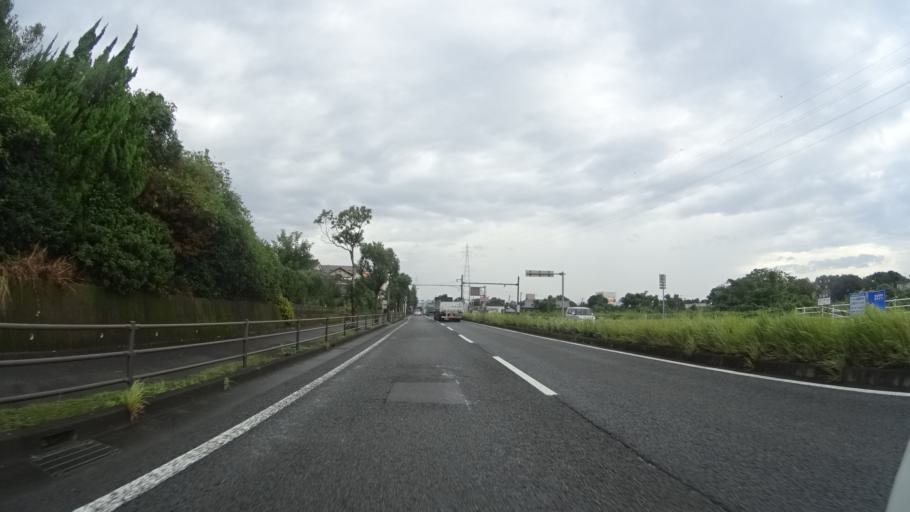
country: JP
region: Kagoshima
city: Kajiki
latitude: 31.7052
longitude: 130.6126
